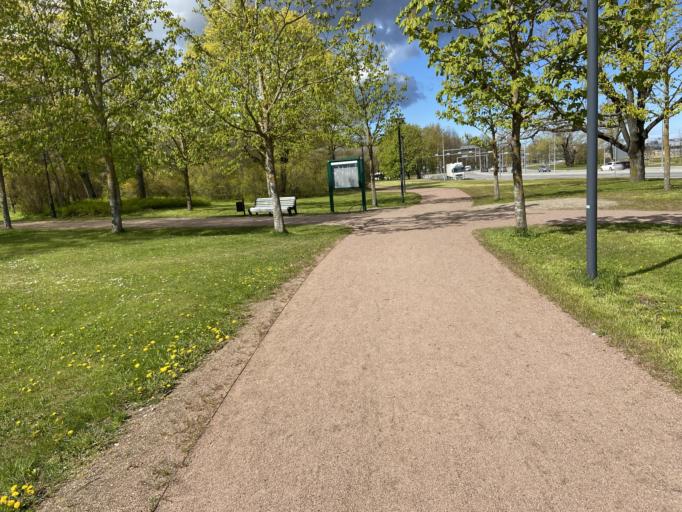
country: EE
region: Harju
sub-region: Tallinna linn
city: Tallinn
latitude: 59.4424
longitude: 24.7936
